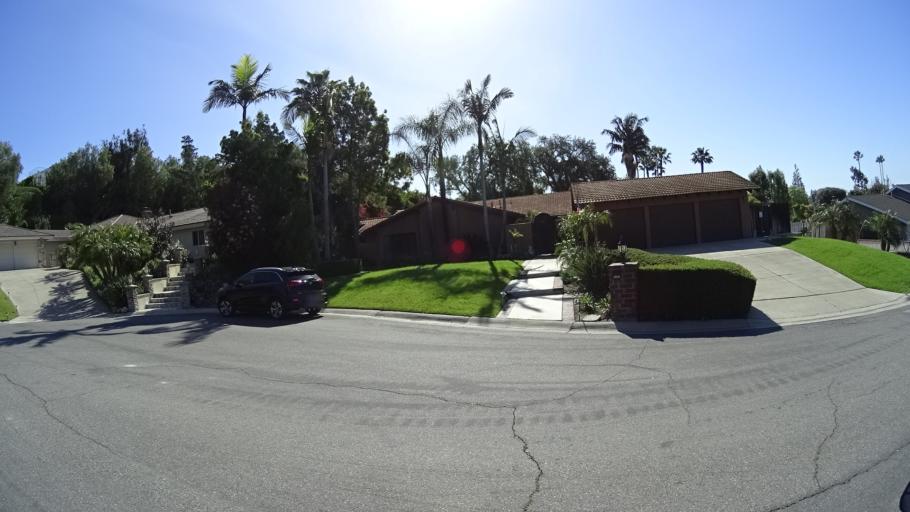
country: US
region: California
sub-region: Orange County
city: Villa Park
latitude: 33.8251
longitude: -117.8200
